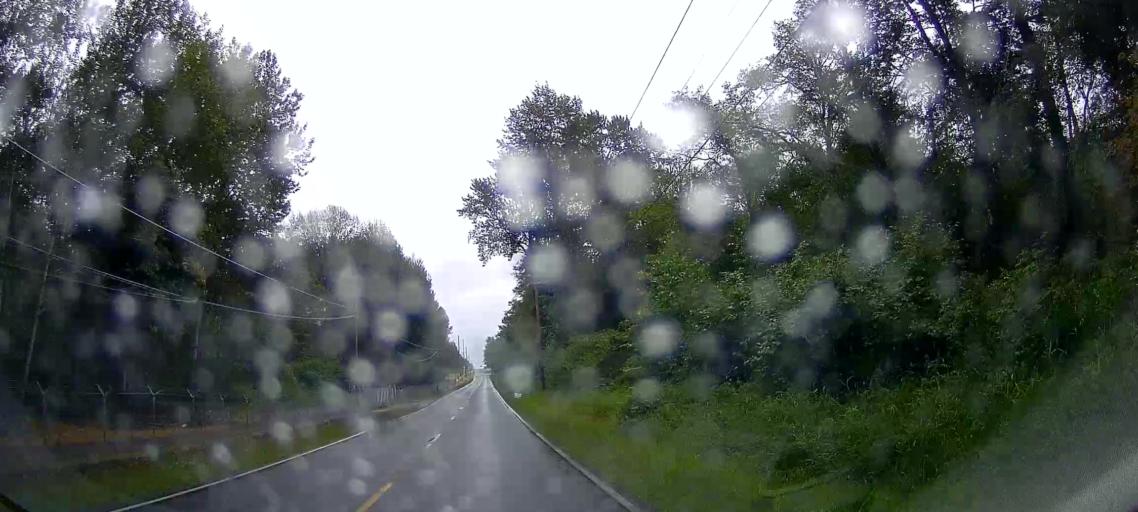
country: US
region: Washington
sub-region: Whatcom County
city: Ferndale
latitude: 48.8195
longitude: -122.6872
